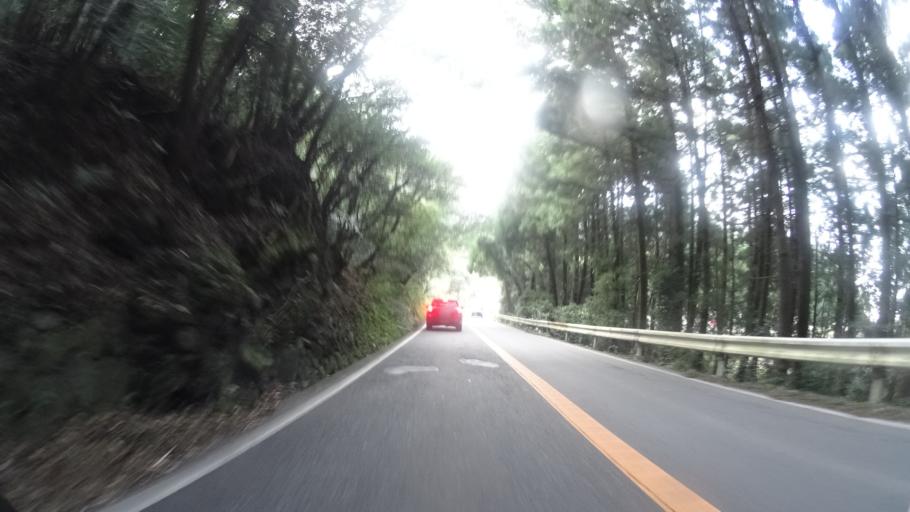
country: JP
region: Oita
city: Beppu
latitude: 33.2887
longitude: 131.4571
